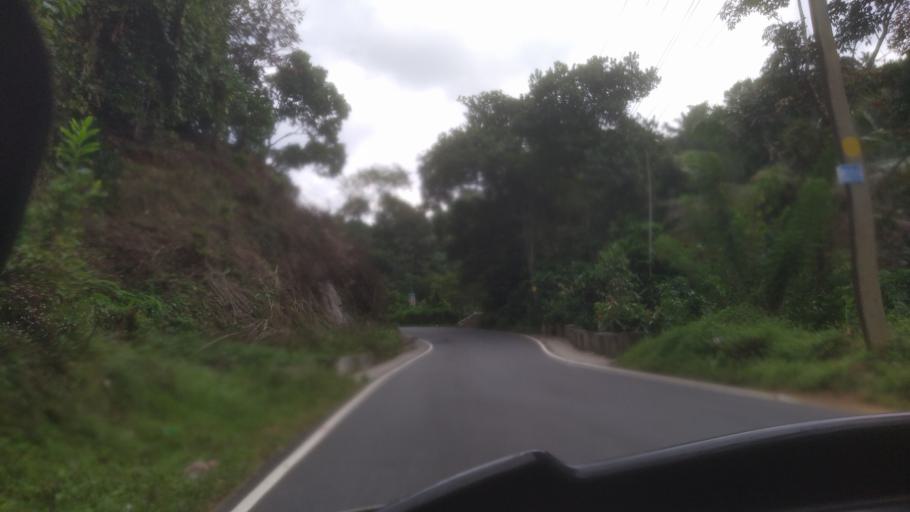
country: IN
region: Kerala
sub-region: Idukki
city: Idukki
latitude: 9.9697
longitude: 76.9995
